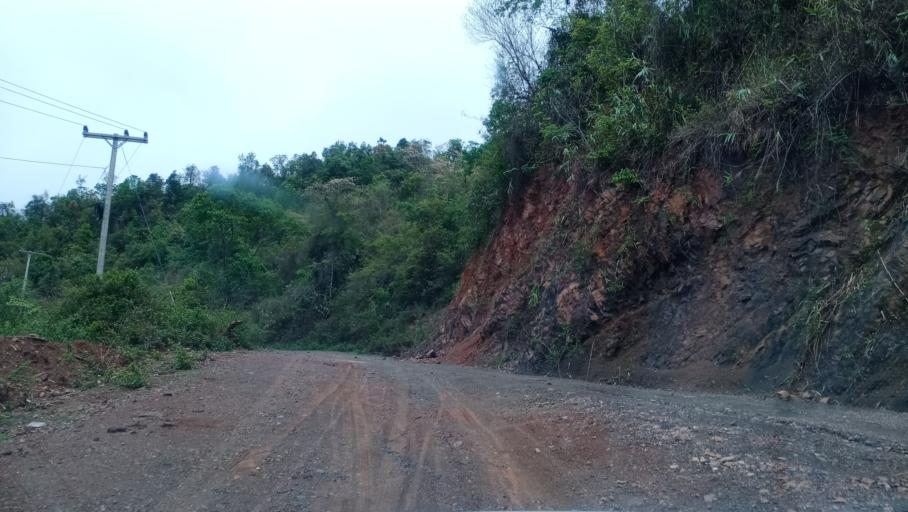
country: LA
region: Phongsali
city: Phongsali
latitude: 21.3478
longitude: 102.0976
